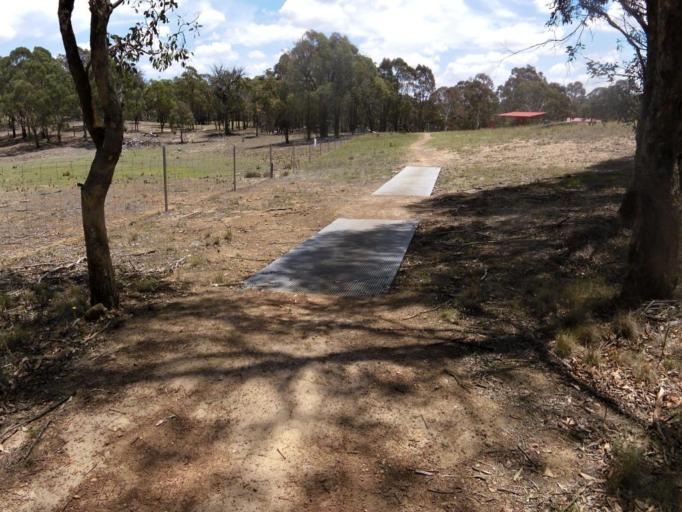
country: AU
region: Australian Capital Territory
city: Kaleen
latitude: -35.1378
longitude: 149.1474
